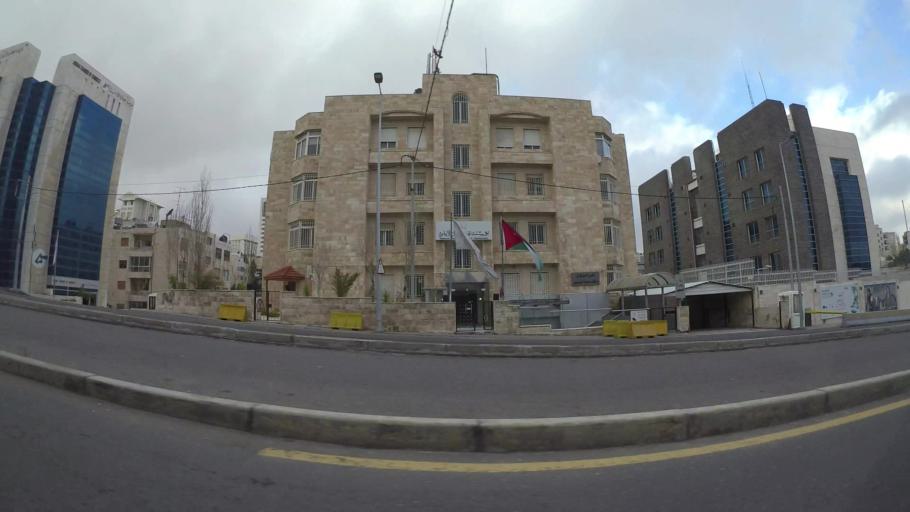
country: JO
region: Amman
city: Wadi as Sir
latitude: 31.9570
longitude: 35.8807
